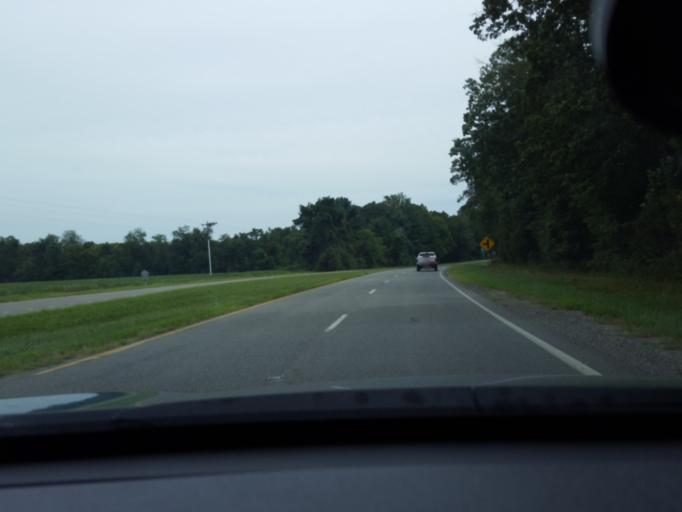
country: US
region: Virginia
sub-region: Caroline County
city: Bowling Green
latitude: 38.0098
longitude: -77.3344
